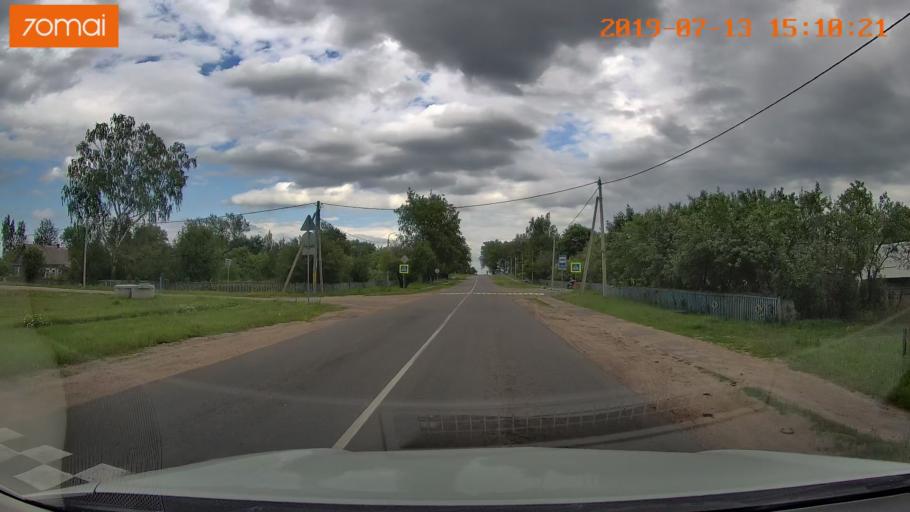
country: BY
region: Mogilev
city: Hlusha
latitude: 53.1703
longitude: 28.7740
